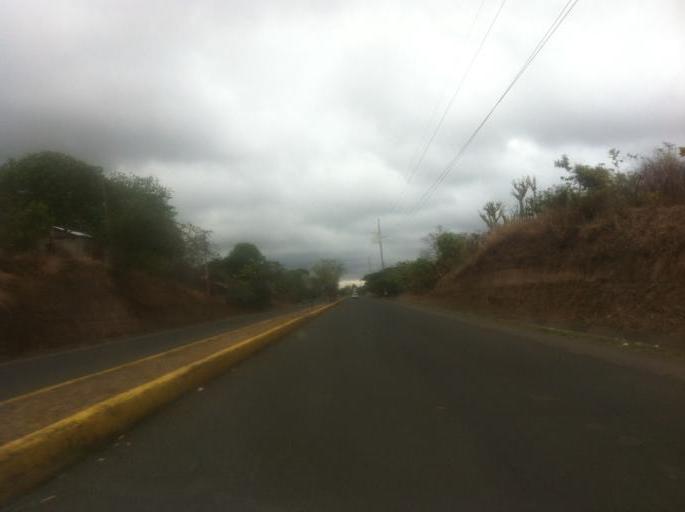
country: NI
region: Granada
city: Granada
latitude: 11.9610
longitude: -85.9939
